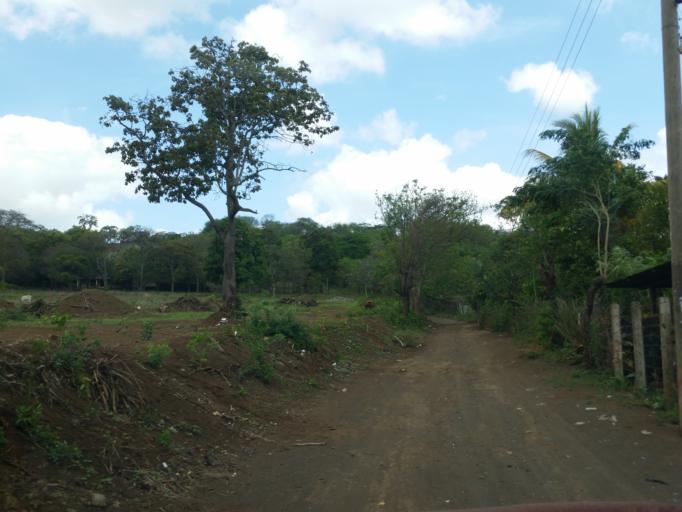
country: NI
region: Masaya
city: Ticuantepe
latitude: 12.0699
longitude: -86.2390
